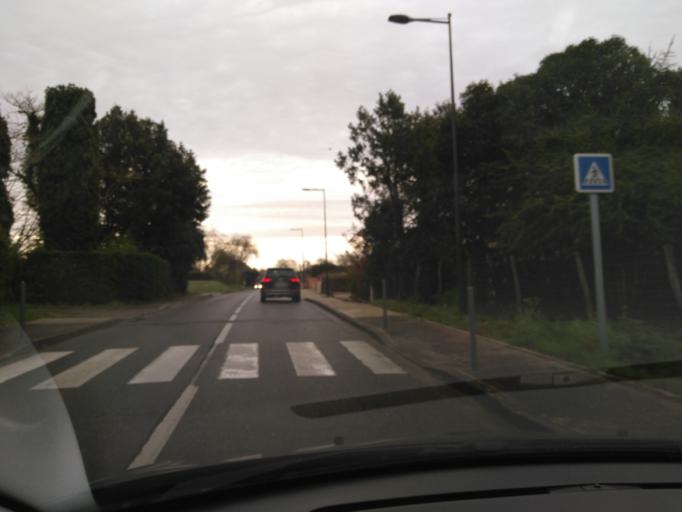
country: FR
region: Midi-Pyrenees
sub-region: Departement de la Haute-Garonne
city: Castelnau-d'Estretefonds
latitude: 43.7801
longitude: 1.3643
